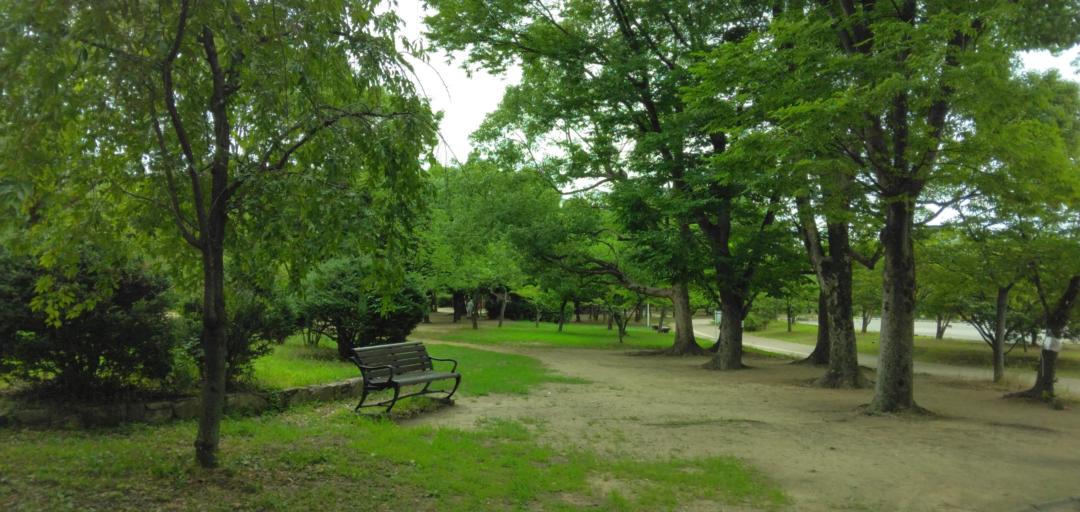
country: JP
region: Osaka
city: Yao
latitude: 34.6572
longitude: 135.5923
